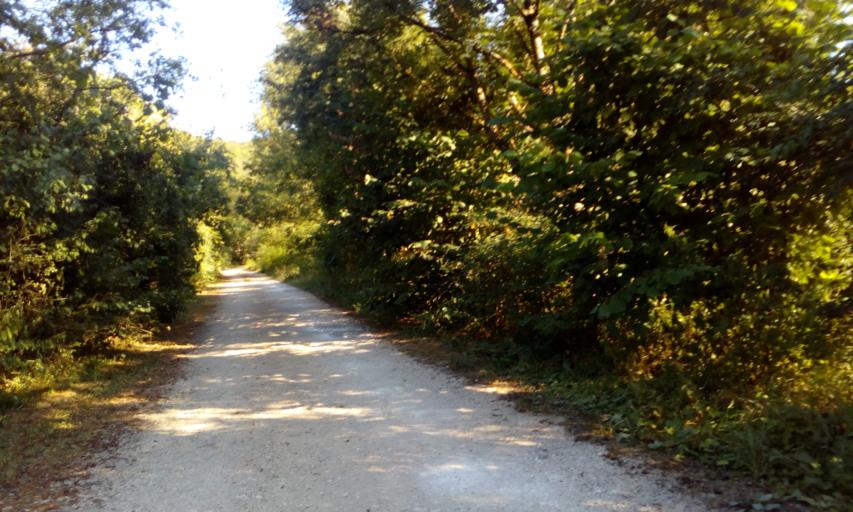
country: FR
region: Lorraine
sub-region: Departement de Meurthe-et-Moselle
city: Pagny-sur-Moselle
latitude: 48.9668
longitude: 5.8872
